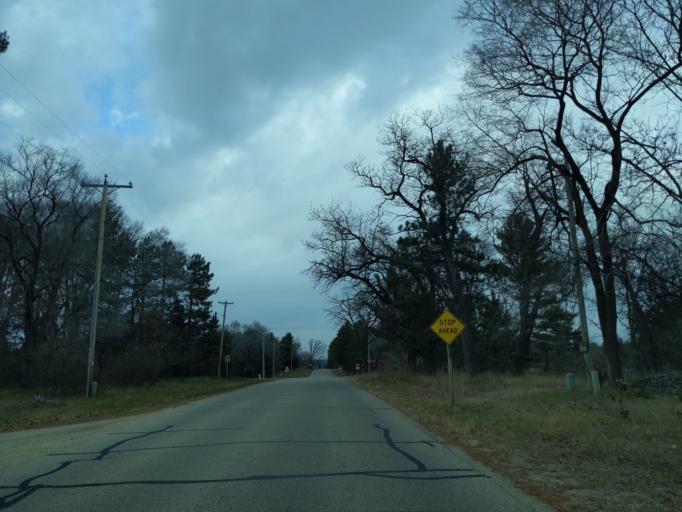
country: US
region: Wisconsin
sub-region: Waushara County
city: Wautoma
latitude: 44.0679
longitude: -89.2773
